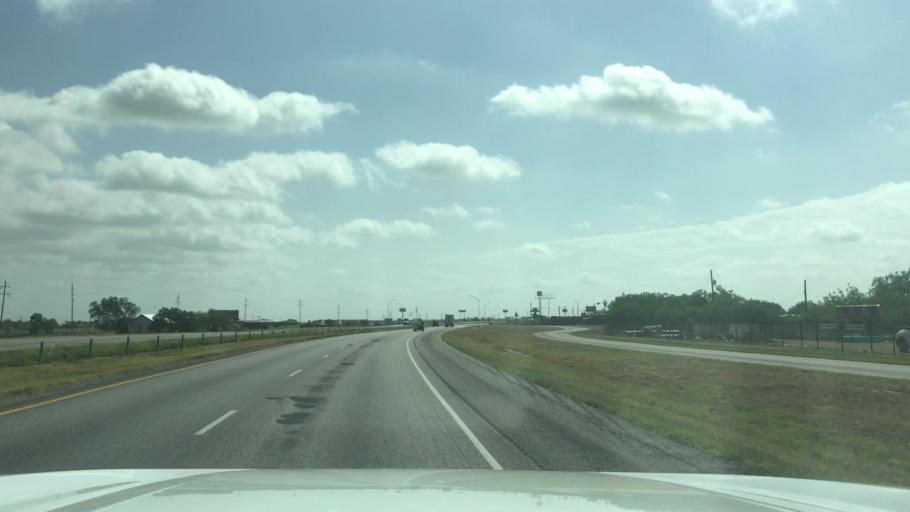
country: US
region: Texas
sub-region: Taylor County
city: Merkel
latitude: 32.4777
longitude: -100.0200
